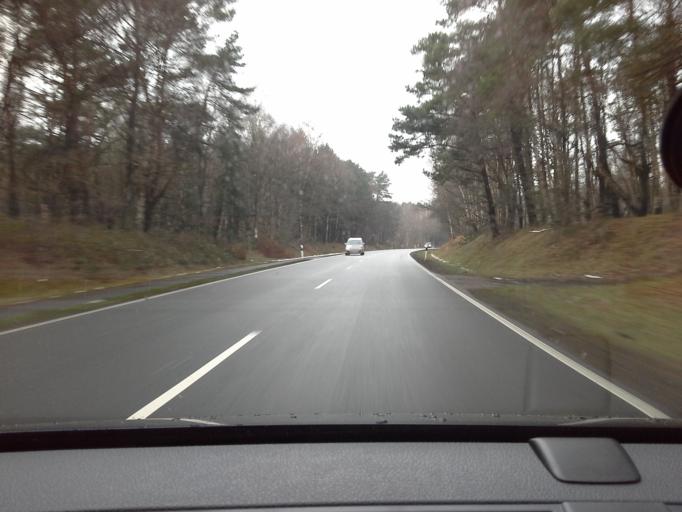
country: DE
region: Schleswig-Holstein
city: Henstedt-Ulzburg
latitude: 53.7455
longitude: 10.0081
